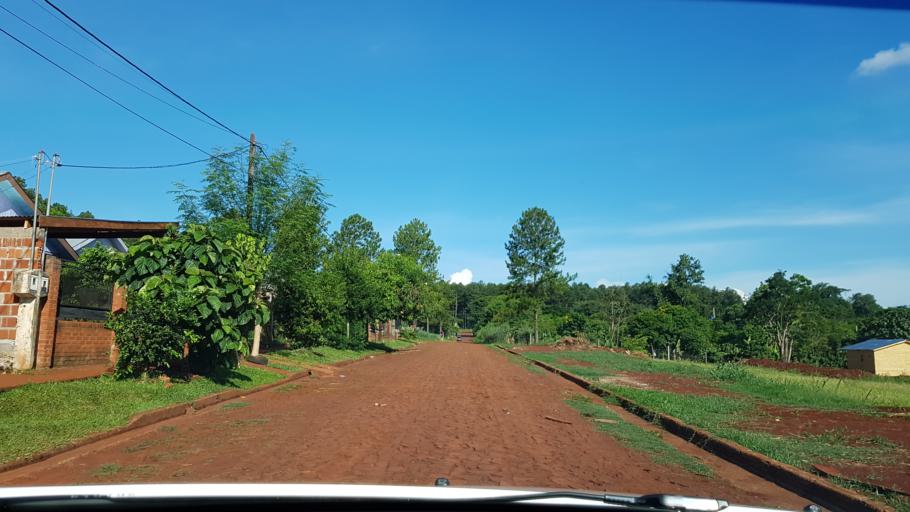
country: AR
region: Misiones
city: Puerto Libertad
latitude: -25.9135
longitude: -54.5815
